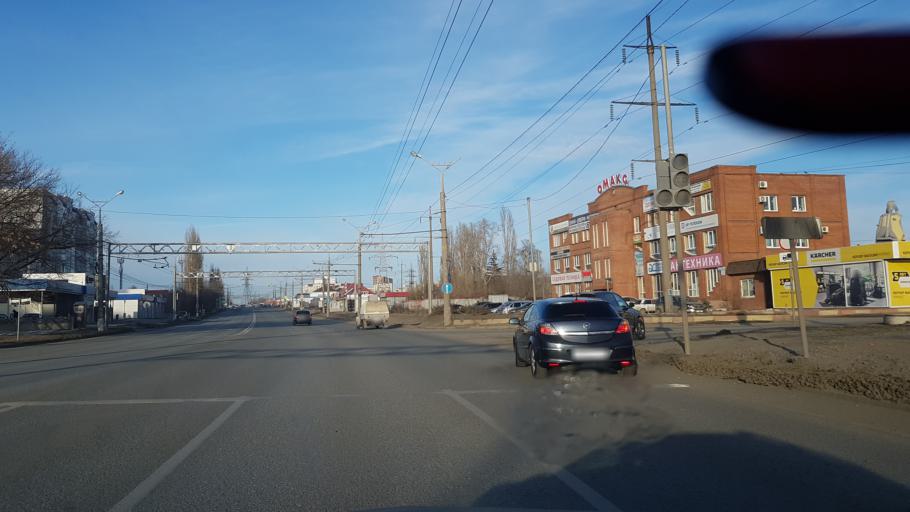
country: RU
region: Samara
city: Tol'yatti
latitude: 53.5311
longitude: 49.3966
